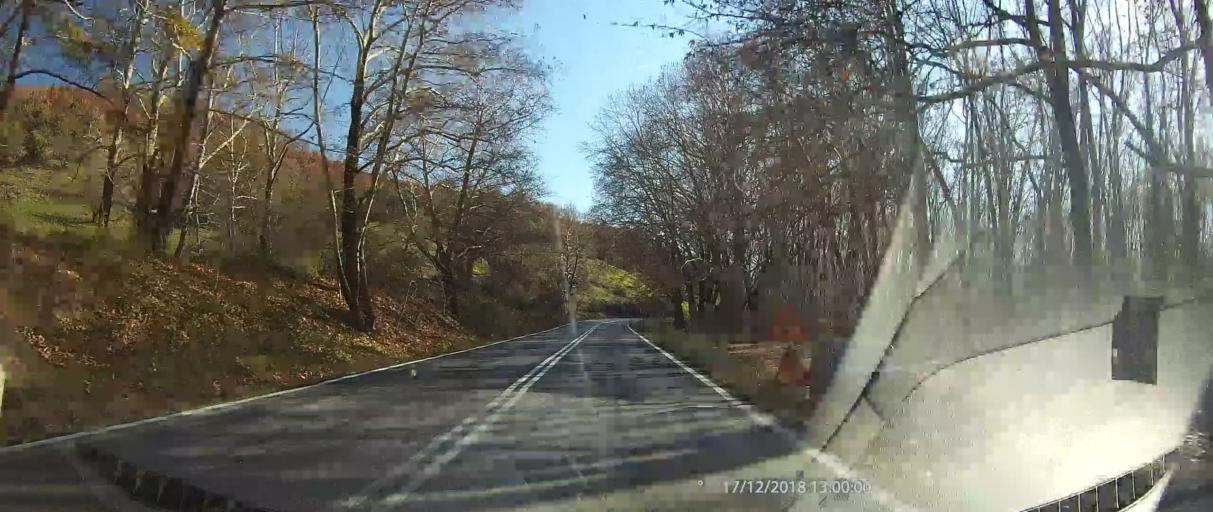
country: GR
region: Thessaly
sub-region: Trikala
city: Kastraki
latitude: 39.7322
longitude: 21.5631
